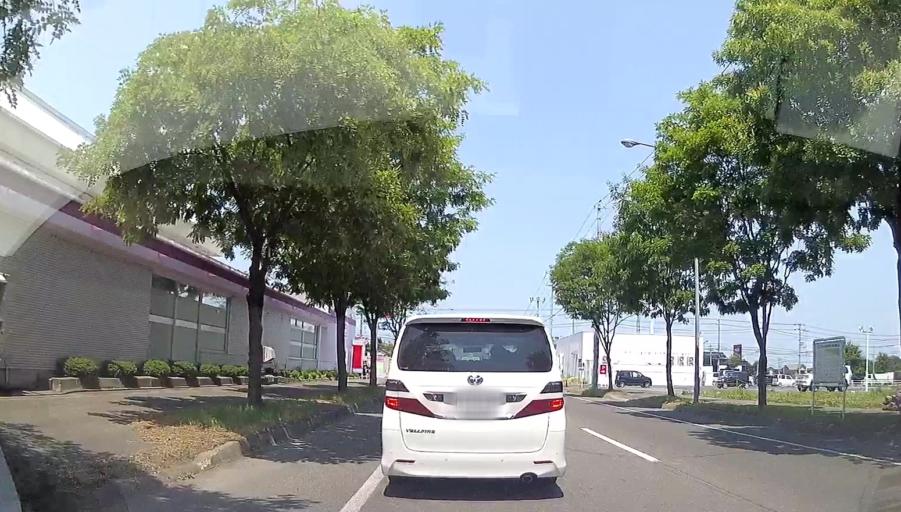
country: JP
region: Hokkaido
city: Obihiro
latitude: 42.8909
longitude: 143.2014
